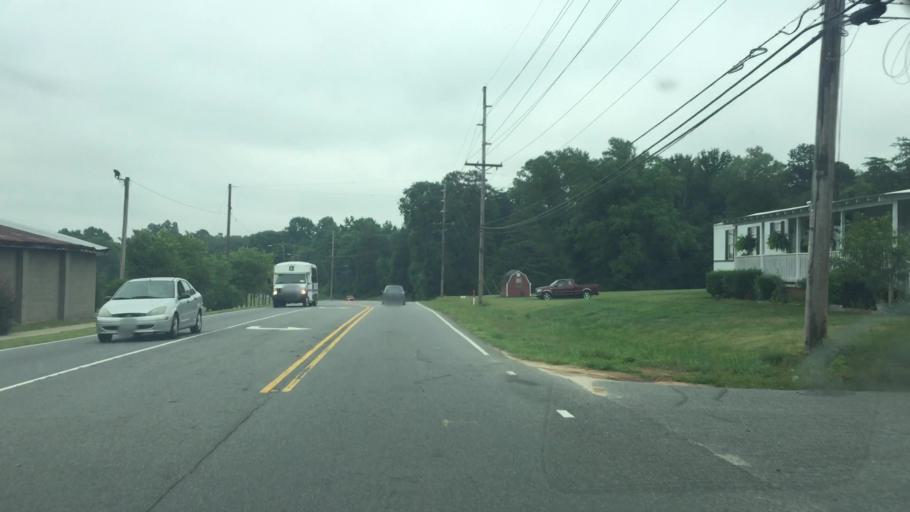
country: US
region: North Carolina
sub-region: Cabarrus County
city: Concord
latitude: 35.4123
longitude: -80.6258
